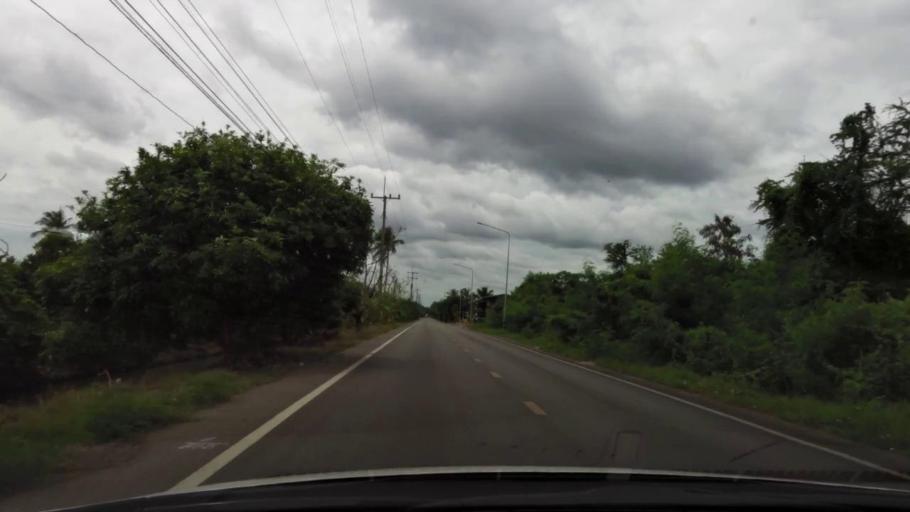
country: TH
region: Ratchaburi
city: Damnoen Saduak
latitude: 13.5538
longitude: 100.0163
